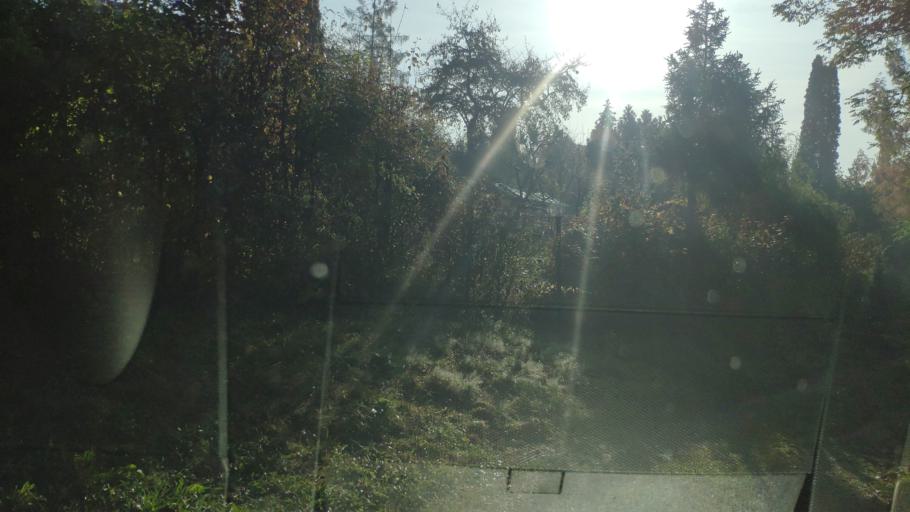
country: SK
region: Kosicky
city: Kosice
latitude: 48.7313
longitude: 21.2212
